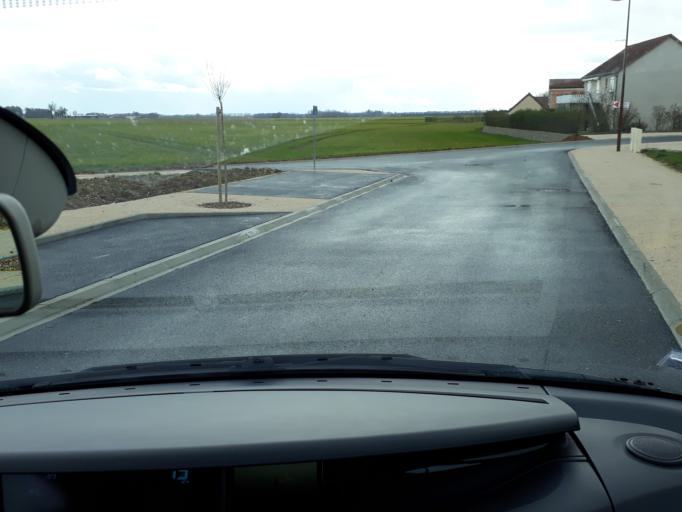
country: FR
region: Bourgogne
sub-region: Departement de la Cote-d'Or
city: Longecourt-en-Plaine
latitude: 47.2076
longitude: 5.1839
